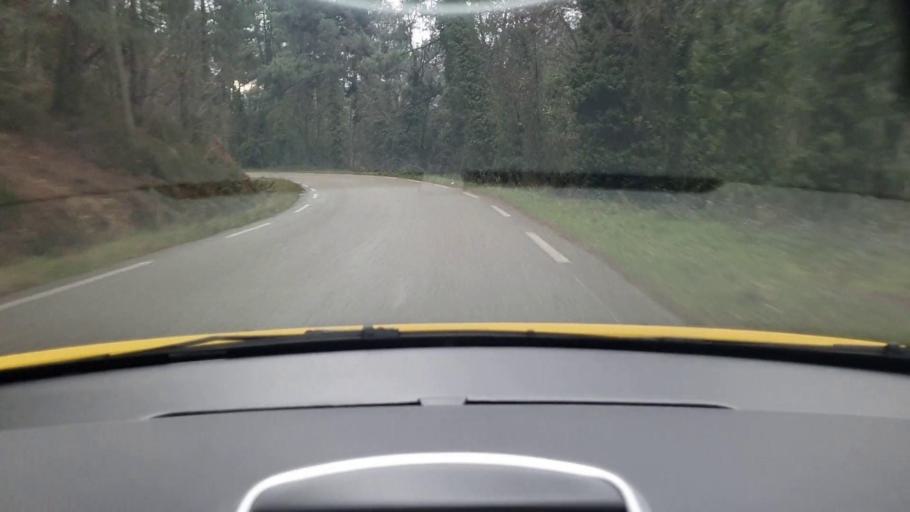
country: FR
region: Languedoc-Roussillon
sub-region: Departement du Gard
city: Besseges
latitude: 44.2644
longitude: 4.0815
